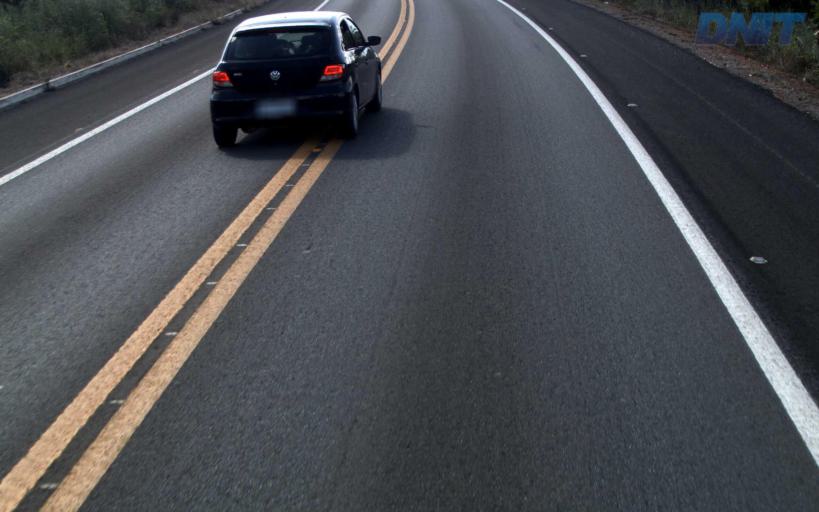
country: BR
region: Goias
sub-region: Padre Bernardo
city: Padre Bernardo
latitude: -15.2109
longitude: -48.5637
